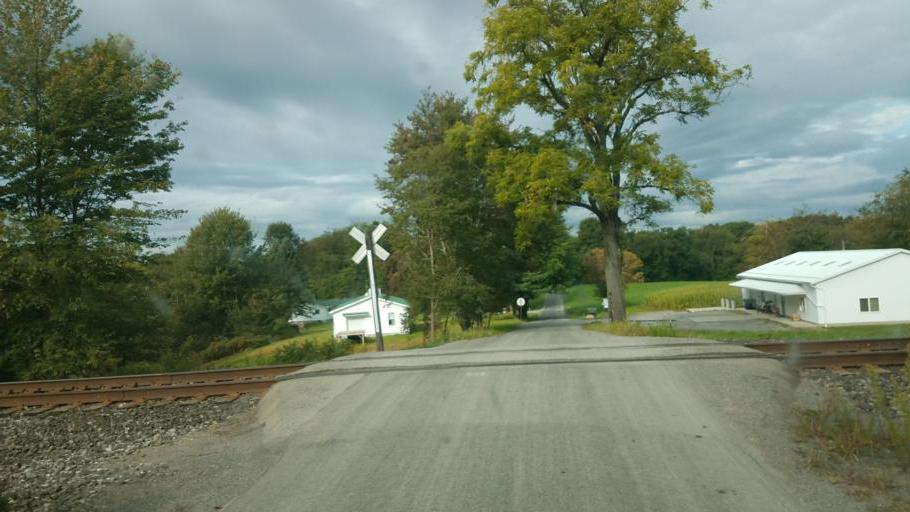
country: US
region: Pennsylvania
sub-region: Mercer County
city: Greenville
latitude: 41.4846
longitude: -80.3392
